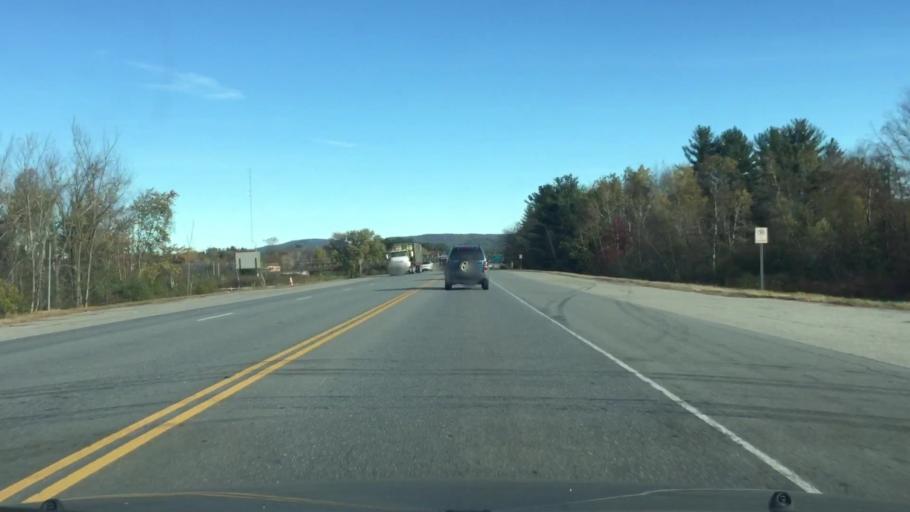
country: US
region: New Hampshire
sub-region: Cheshire County
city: Keene
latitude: 42.9265
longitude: -72.2993
